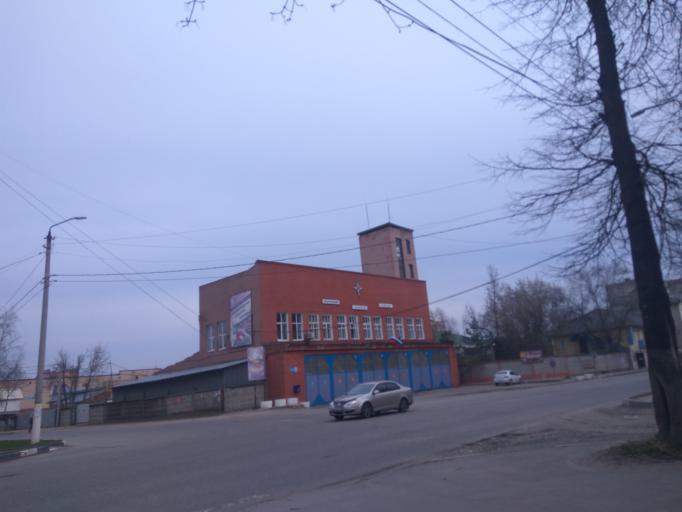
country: RU
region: Vladimir
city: Aleksandrov
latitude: 56.3989
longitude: 38.7137
